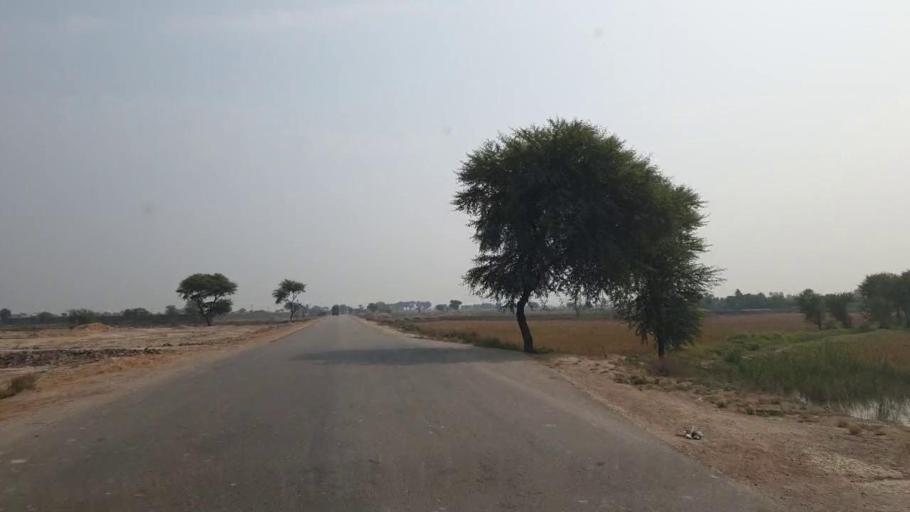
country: PK
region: Sindh
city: Matli
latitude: 25.0559
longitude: 68.6751
